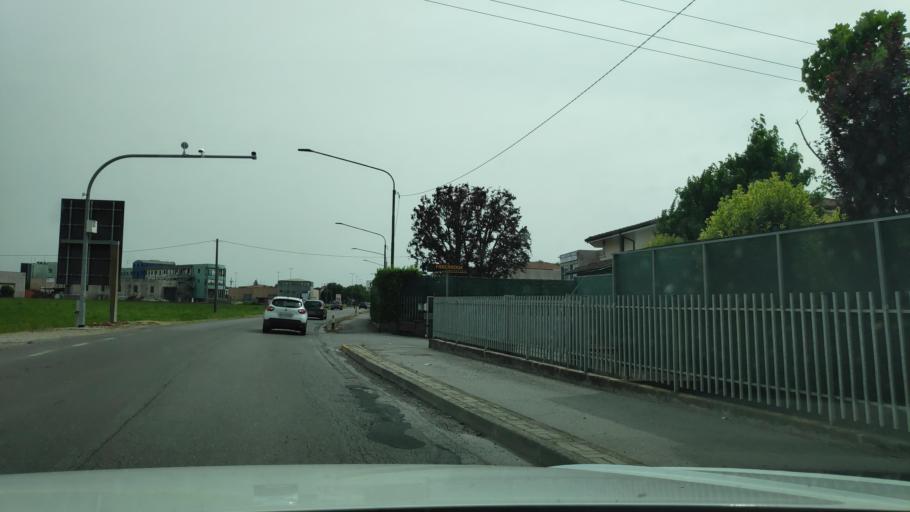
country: IT
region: Lombardy
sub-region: Provincia di Brescia
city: Orzinuovi
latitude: 45.4121
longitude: 9.9273
